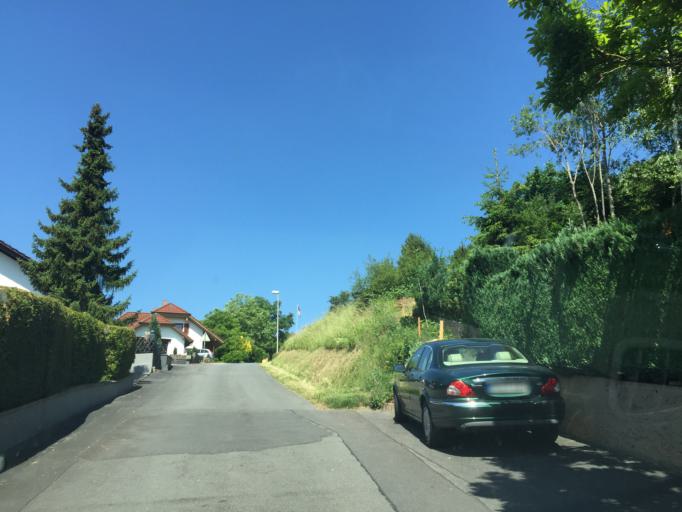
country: DE
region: Bavaria
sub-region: Regierungsbezirk Unterfranken
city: Weilbach
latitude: 49.6425
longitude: 9.2434
